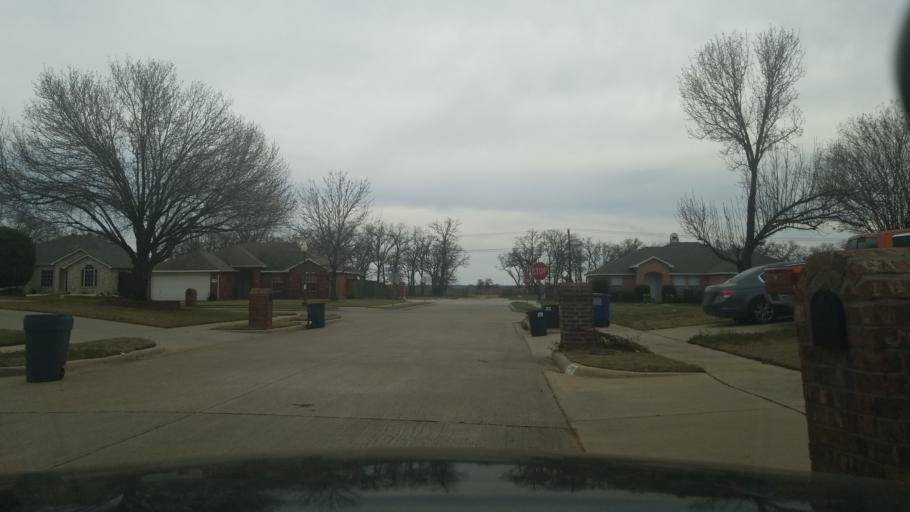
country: US
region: Texas
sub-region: Denton County
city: Hickory Creek
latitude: 33.1310
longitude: -97.0586
